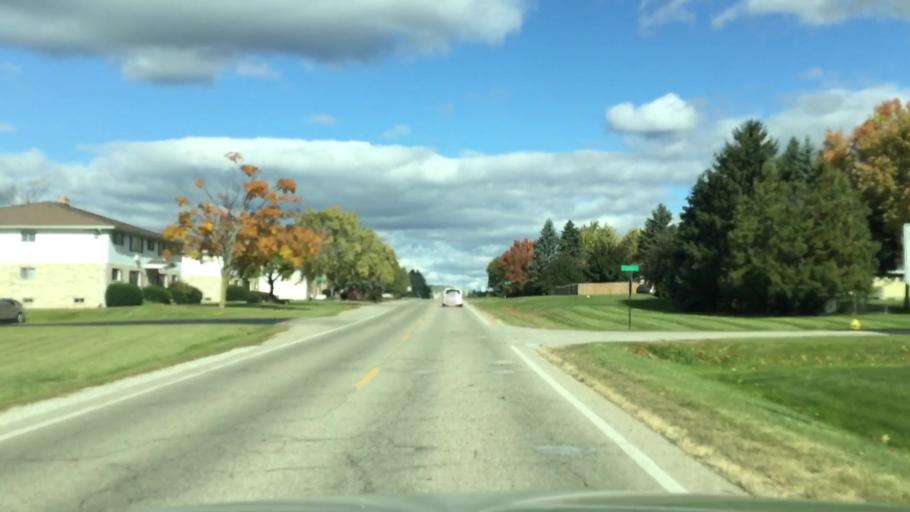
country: US
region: Michigan
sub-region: Lapeer County
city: Lapeer
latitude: 43.0609
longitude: -83.3333
